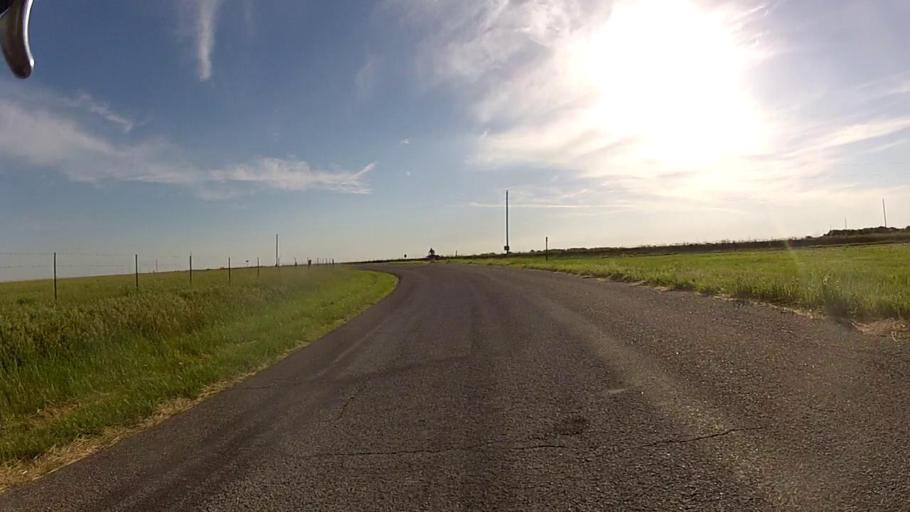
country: US
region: Kansas
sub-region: Cowley County
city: Arkansas City
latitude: 37.0489
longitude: -96.8235
